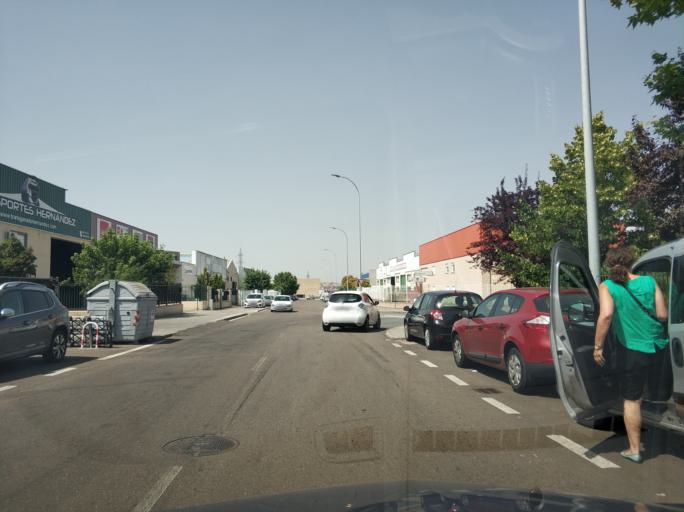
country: ES
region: Castille and Leon
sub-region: Provincia de Salamanca
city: Carbajosa de la Sagrada
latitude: 40.9384
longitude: -5.6669
